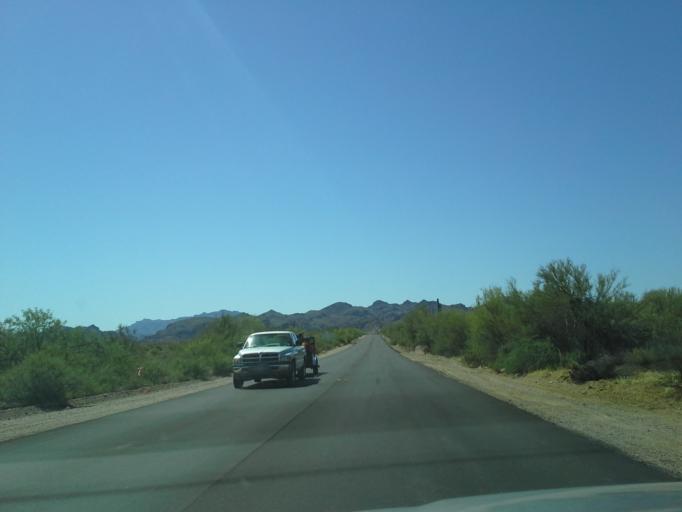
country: US
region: Arizona
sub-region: Maricopa County
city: Fountain Hills
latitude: 33.5936
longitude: -111.5439
